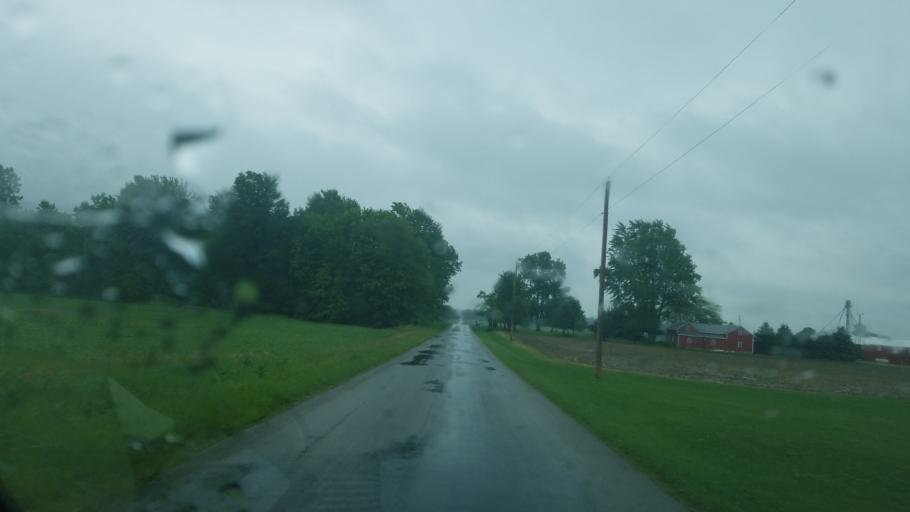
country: US
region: Ohio
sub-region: Huron County
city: Plymouth
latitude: 40.9453
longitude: -82.7533
